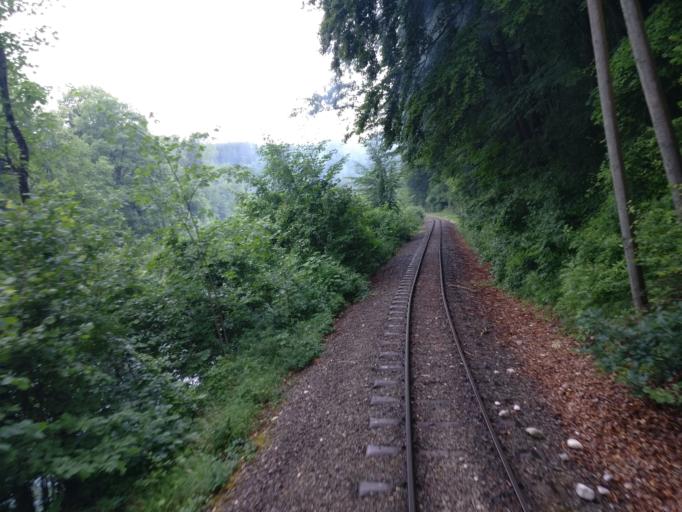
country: AT
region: Upper Austria
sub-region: Politischer Bezirk Steyr-Land
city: Waldneukirchen
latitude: 47.9927
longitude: 14.2800
